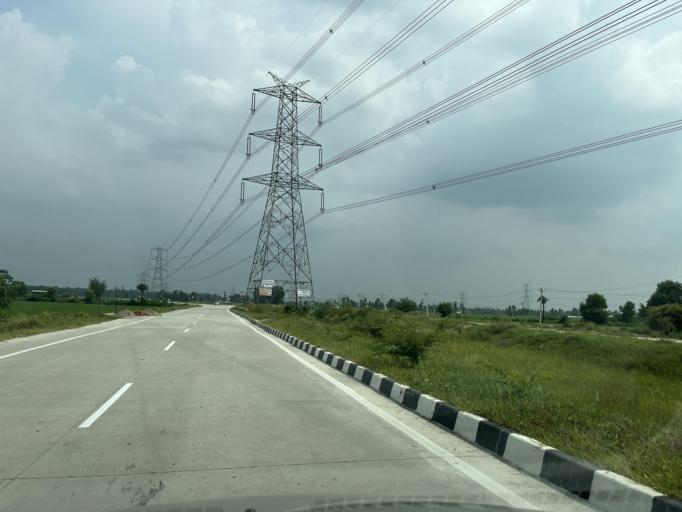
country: IN
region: Uttarakhand
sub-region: Udham Singh Nagar
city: Jaspur
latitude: 29.2848
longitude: 78.8578
